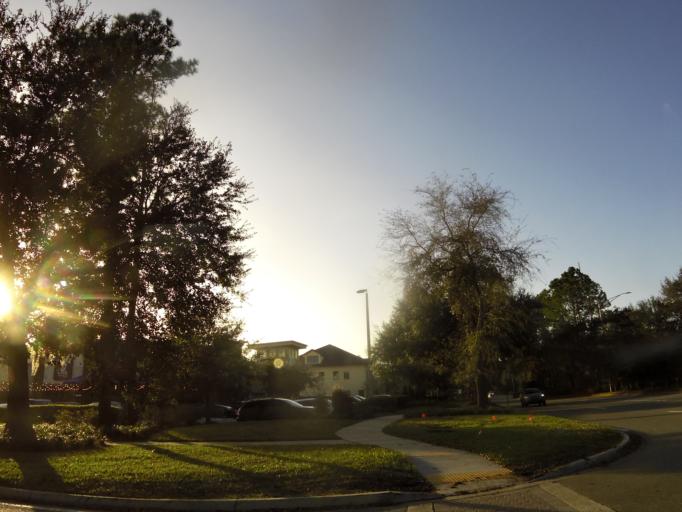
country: US
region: Florida
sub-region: Duval County
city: Jacksonville
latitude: 30.2680
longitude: -81.5546
